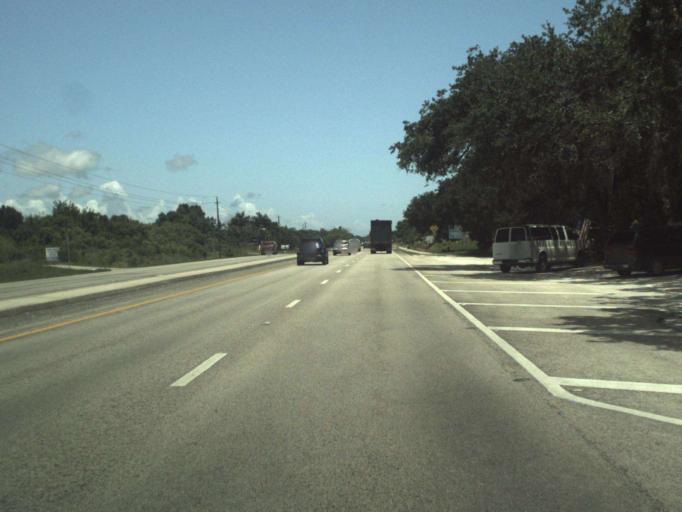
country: US
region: Florida
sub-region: Indian River County
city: Sebastian
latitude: 27.7979
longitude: -80.4604
